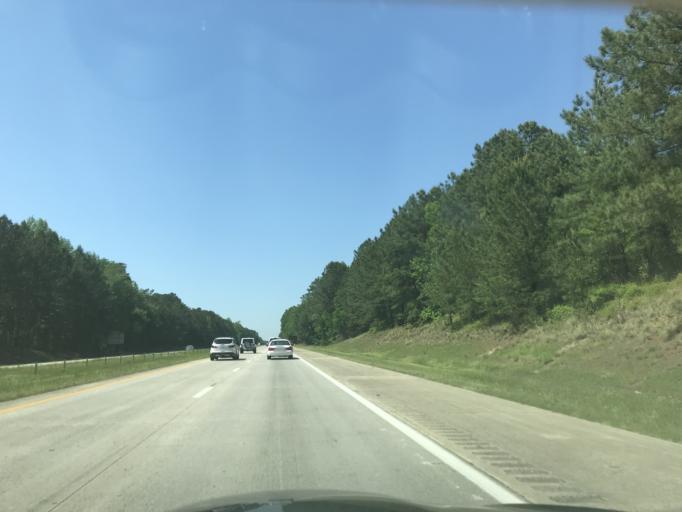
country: US
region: North Carolina
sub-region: Johnston County
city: Benson
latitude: 35.5248
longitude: -78.5635
